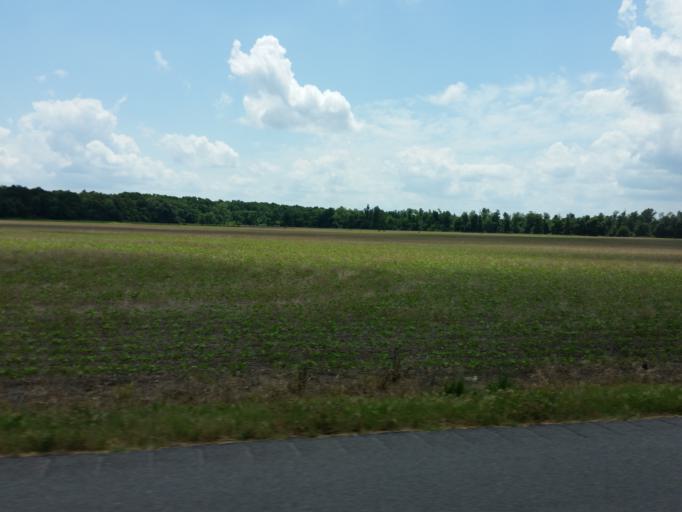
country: US
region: Tennessee
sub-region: Lake County
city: Tiptonville
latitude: 36.5065
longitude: -89.3528
